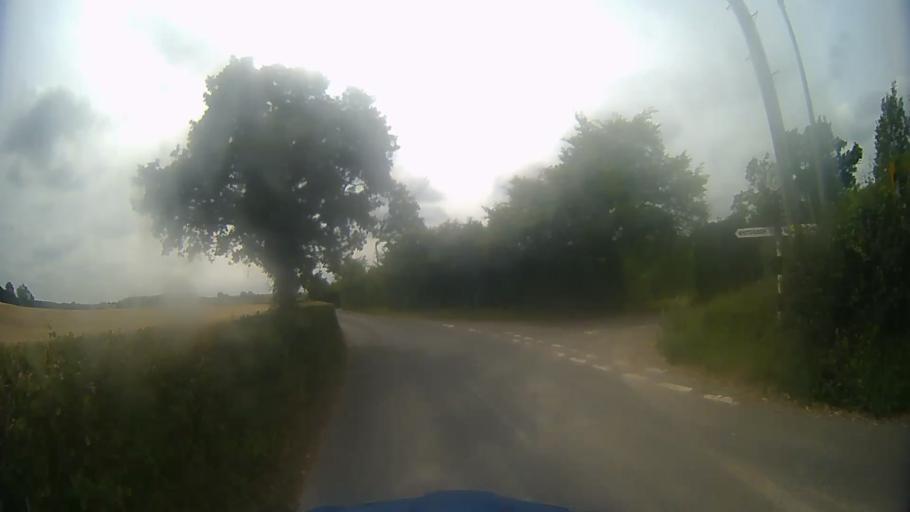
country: GB
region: England
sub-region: Hampshire
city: Overton
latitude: 51.2592
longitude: -1.3238
